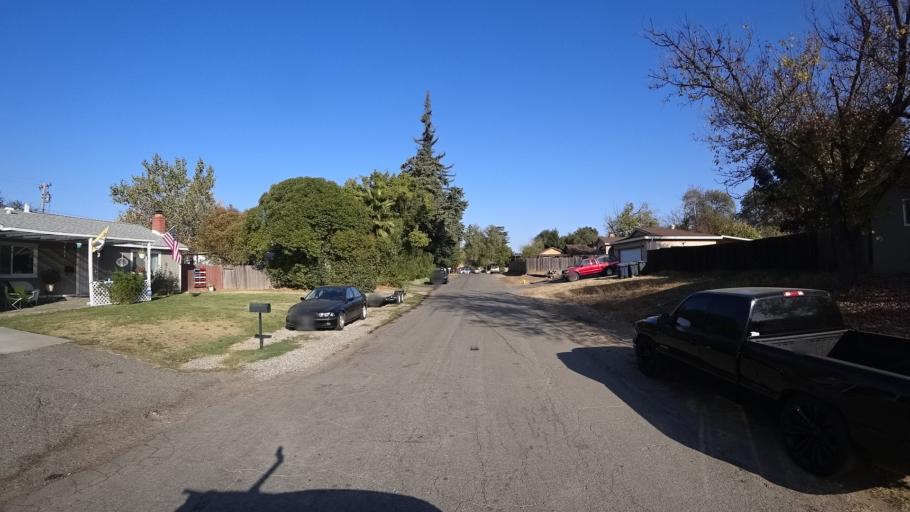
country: US
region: California
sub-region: Sacramento County
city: Citrus Heights
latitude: 38.6981
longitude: -121.2553
